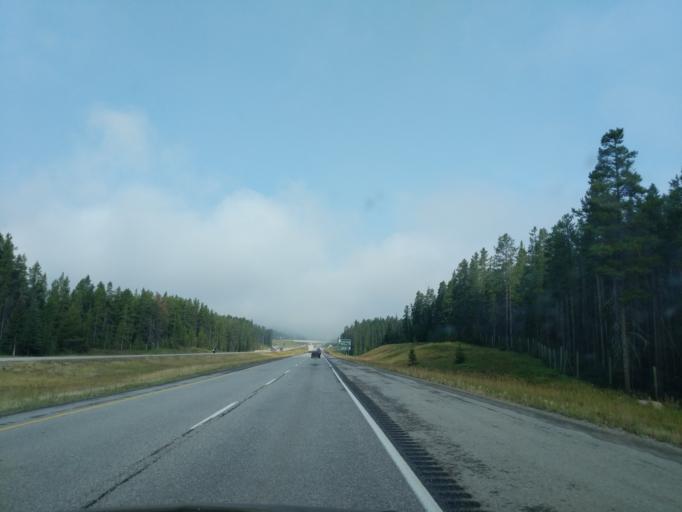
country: CA
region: Alberta
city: Banff
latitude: 51.2614
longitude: -115.9192
